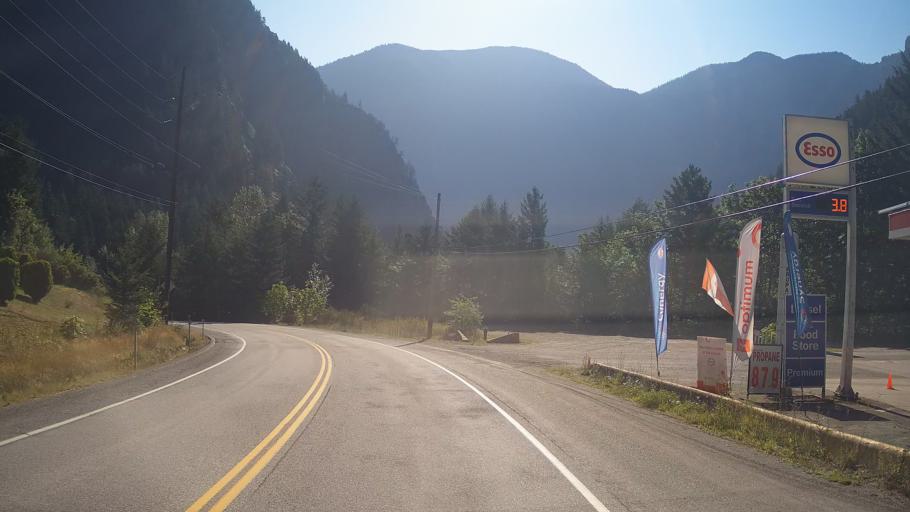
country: CA
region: British Columbia
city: Hope
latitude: 49.5628
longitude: -121.4286
